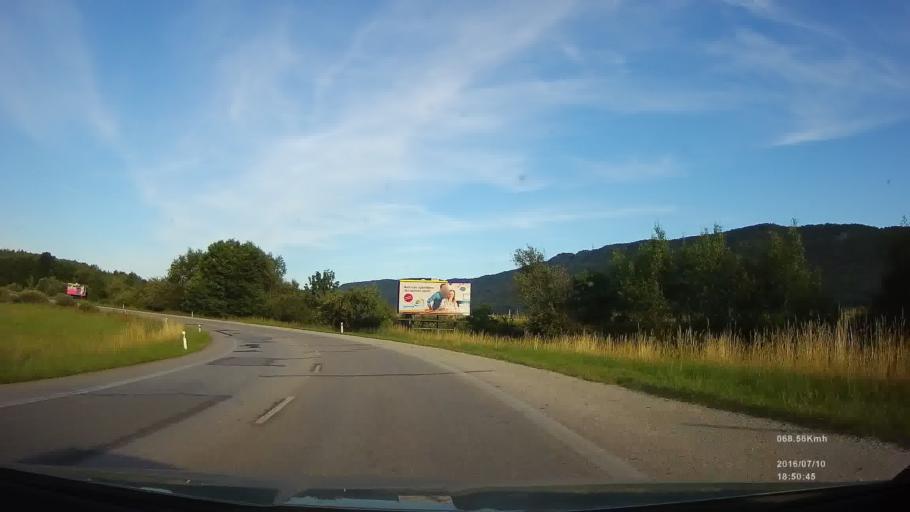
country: SK
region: Kosicky
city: Roznava
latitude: 48.6405
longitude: 20.5250
